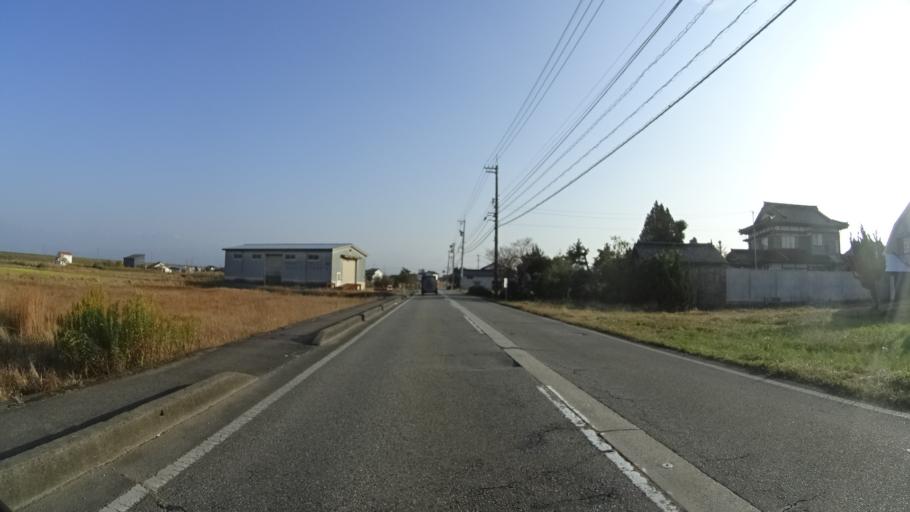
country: JP
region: Toyama
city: Toyama-shi
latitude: 36.6906
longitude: 137.2702
